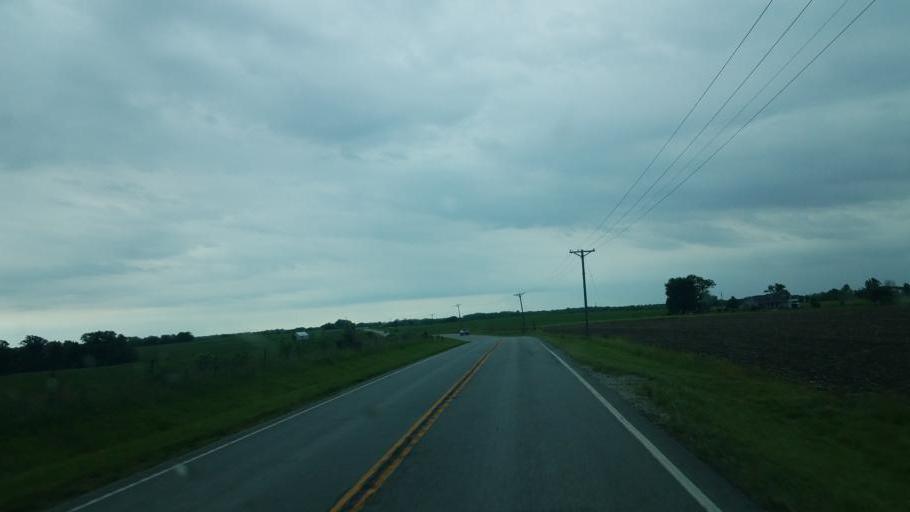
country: US
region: Missouri
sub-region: Cooper County
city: Boonville
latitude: 38.8527
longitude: -92.6350
